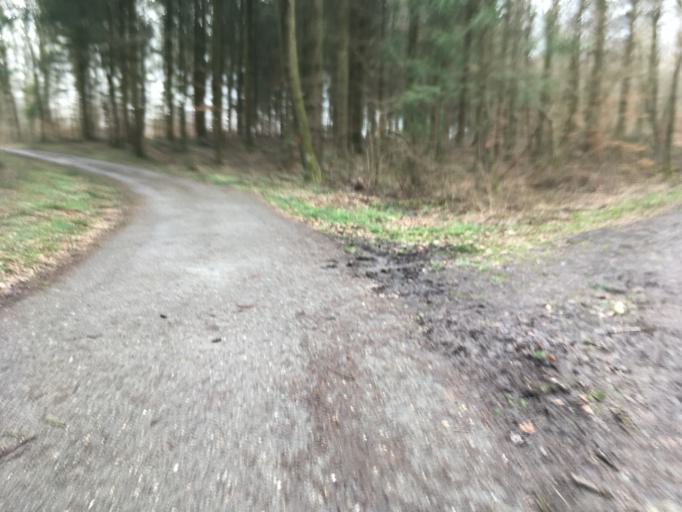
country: DE
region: Baden-Wuerttemberg
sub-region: Regierungsbezirk Stuttgart
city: Schwaigern
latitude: 49.1229
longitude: 9.0861
